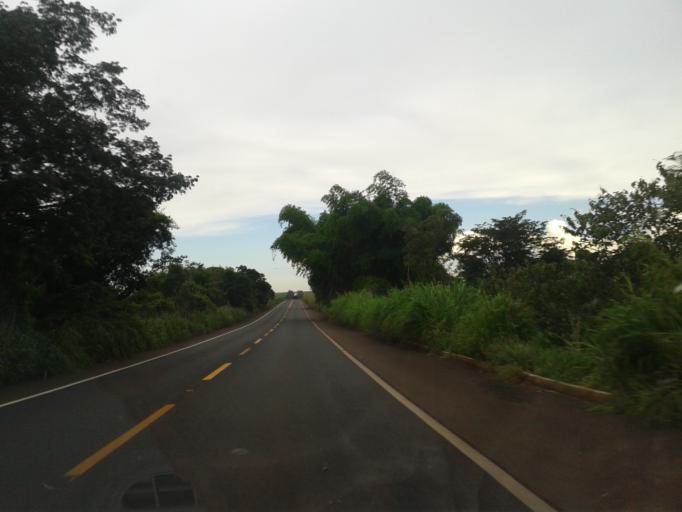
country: BR
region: Minas Gerais
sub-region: Santa Vitoria
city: Santa Vitoria
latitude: -18.9074
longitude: -50.2102
